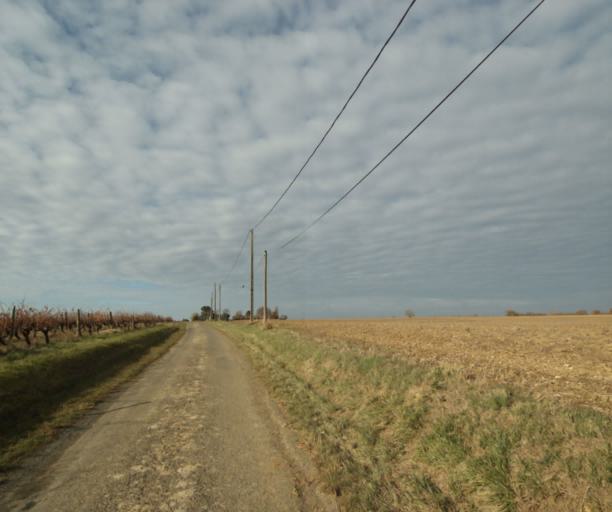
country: FR
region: Poitou-Charentes
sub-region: Departement de la Charente-Maritime
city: Corme-Royal
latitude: 45.7302
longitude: -0.8070
